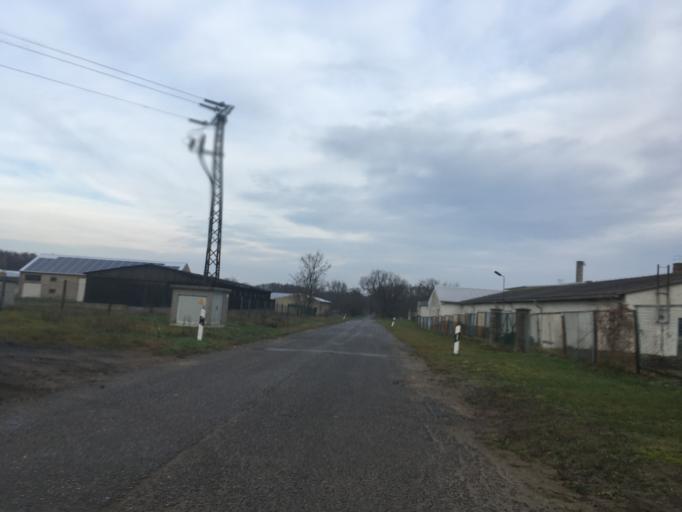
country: DE
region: Brandenburg
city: Seelow
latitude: 52.5624
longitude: 14.3481
